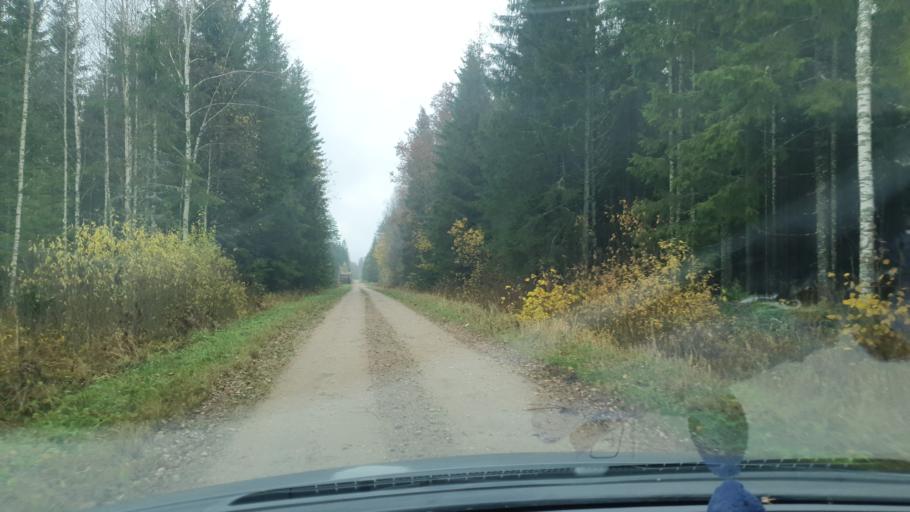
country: EE
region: Viljandimaa
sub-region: Karksi vald
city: Karksi-Nuia
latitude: 57.9828
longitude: 25.6341
